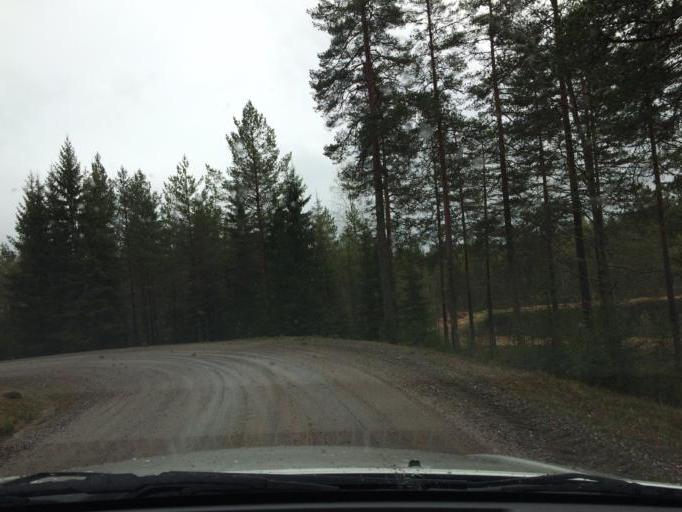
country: SE
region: OErebro
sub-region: Hallefors Kommun
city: Haellefors
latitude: 60.0153
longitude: 14.5883
